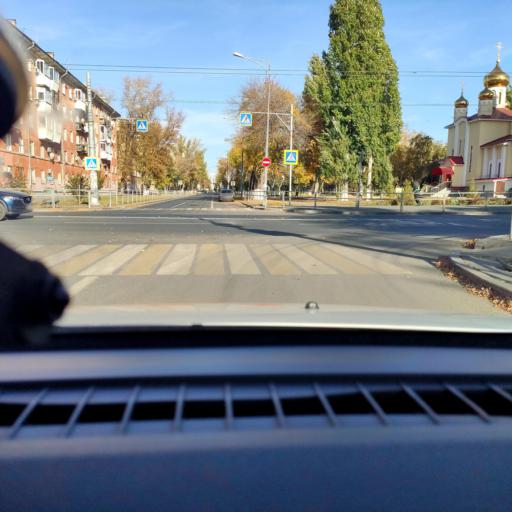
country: RU
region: Samara
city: Samara
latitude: 53.2052
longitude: 50.1628
